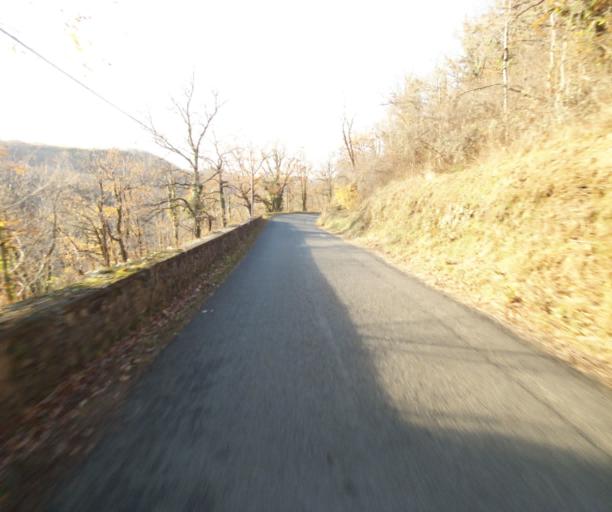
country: FR
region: Limousin
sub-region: Departement de la Correze
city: Laguenne
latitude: 45.2377
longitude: 1.8020
